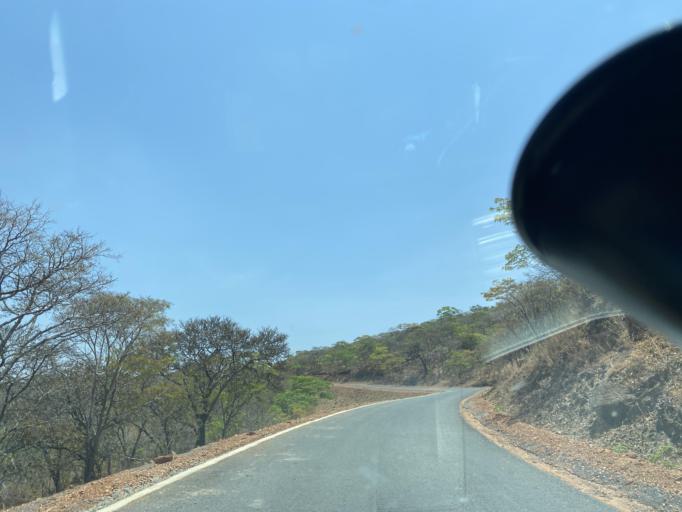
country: ZM
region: Lusaka
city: Kafue
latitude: -15.8591
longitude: 28.4231
